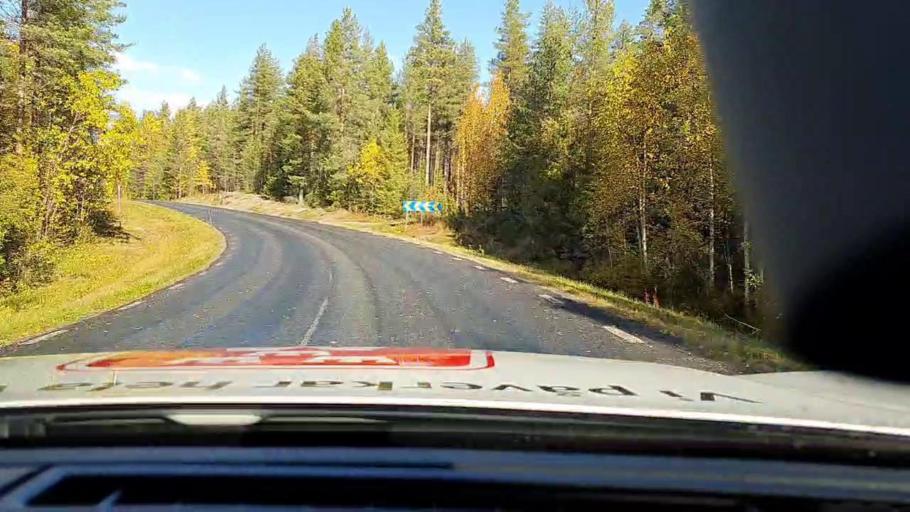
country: SE
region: Vaesterbotten
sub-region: Skelleftea Kommun
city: Langsele
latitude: 65.0017
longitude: 20.0914
